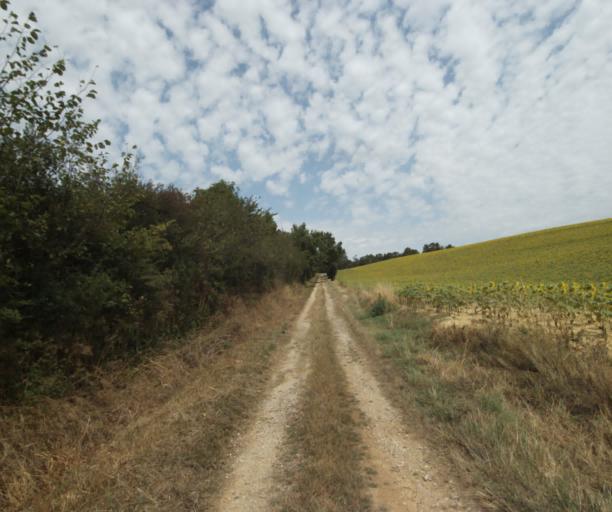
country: FR
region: Midi-Pyrenees
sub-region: Departement de la Haute-Garonne
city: Saint-Felix-Lauragais
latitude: 43.4470
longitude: 1.8920
